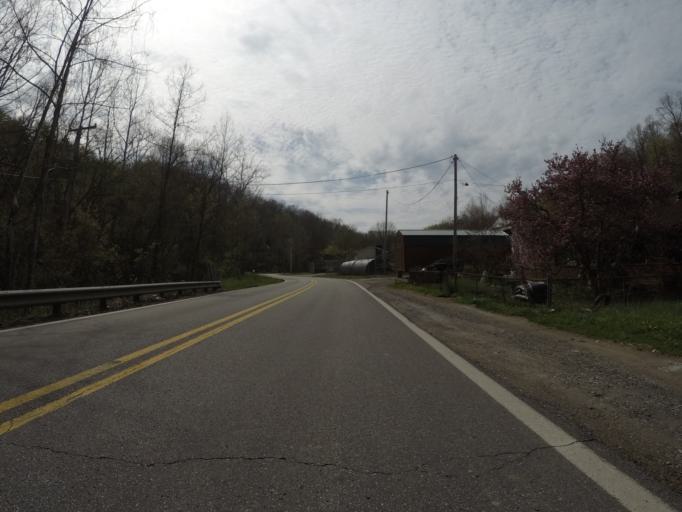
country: US
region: West Virginia
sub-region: Cabell County
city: Pea Ridge
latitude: 38.3643
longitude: -82.3738
